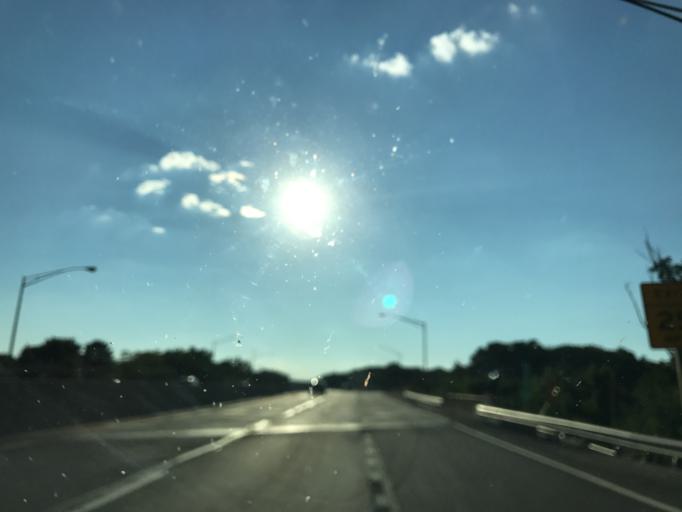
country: US
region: Pennsylvania
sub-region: Bucks County
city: Bristol
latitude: 40.1222
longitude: -74.8484
